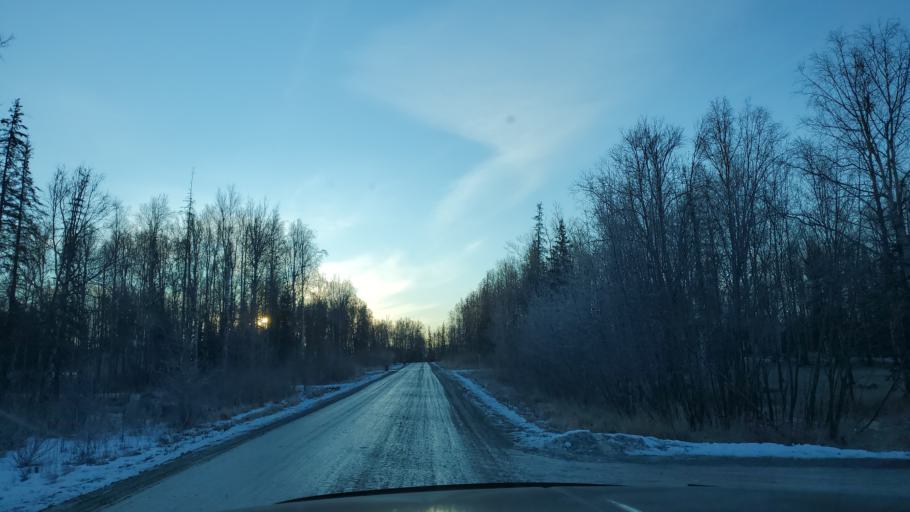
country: US
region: Alaska
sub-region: Matanuska-Susitna Borough
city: Lakes
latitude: 61.6546
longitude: -149.3323
